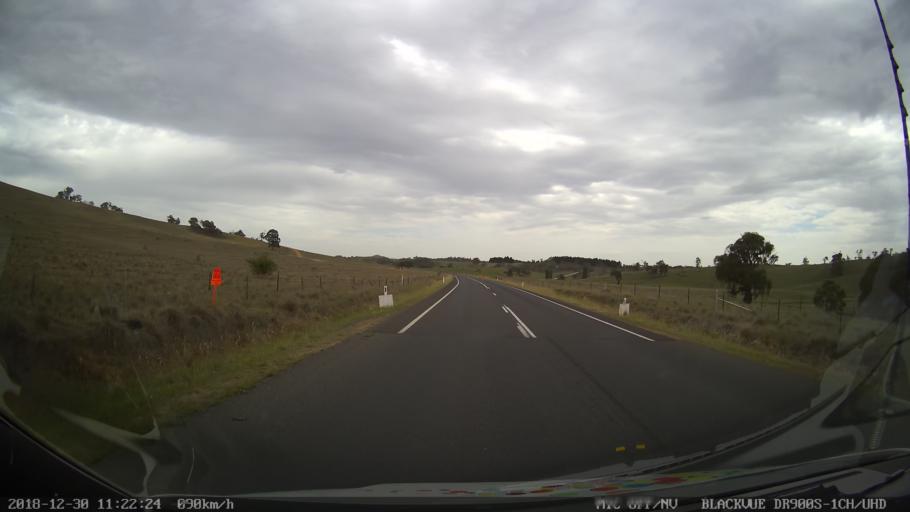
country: AU
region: New South Wales
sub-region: Snowy River
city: Jindabyne
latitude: -36.5002
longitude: 148.6711
